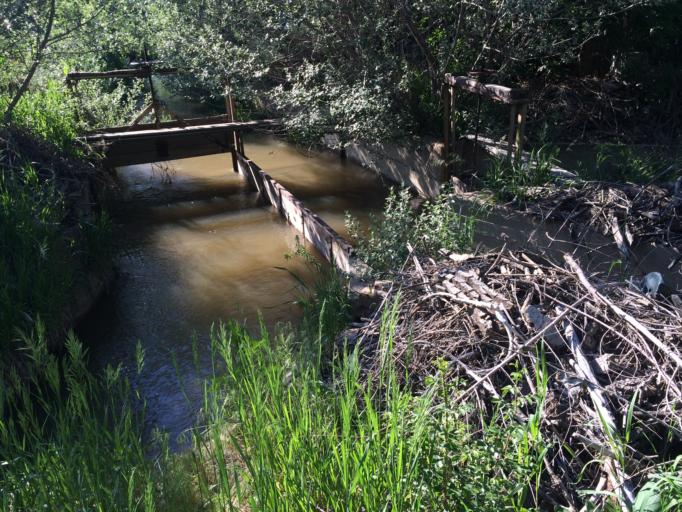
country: US
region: Colorado
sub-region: Boulder County
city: Lafayette
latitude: 40.0155
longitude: -105.1045
